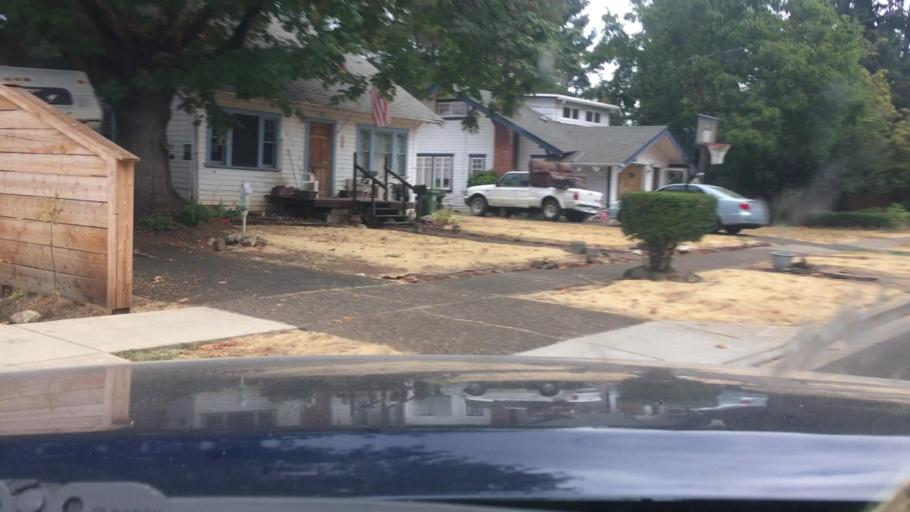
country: US
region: Oregon
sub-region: Lane County
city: Cottage Grove
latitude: 43.7963
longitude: -123.0575
